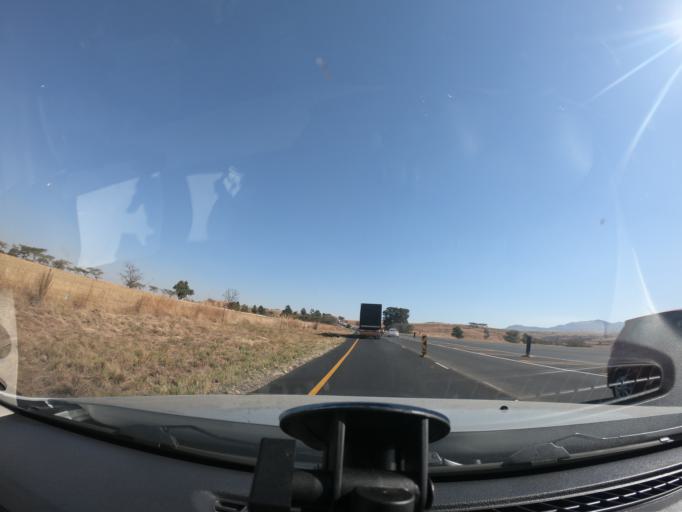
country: ZA
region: KwaZulu-Natal
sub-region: uThukela District Municipality
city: Bergville
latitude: -28.4344
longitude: 29.4769
